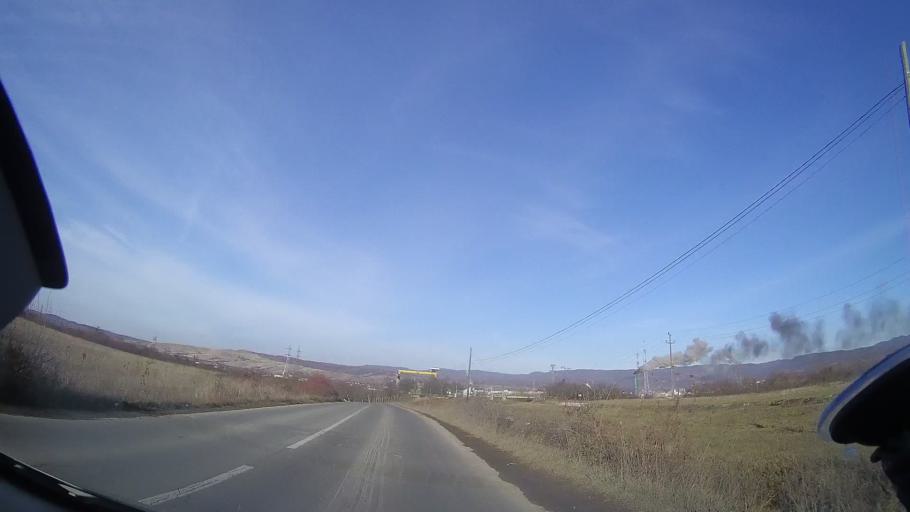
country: RO
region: Bihor
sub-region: Comuna Astileu
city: Astileu
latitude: 47.0404
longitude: 22.3914
